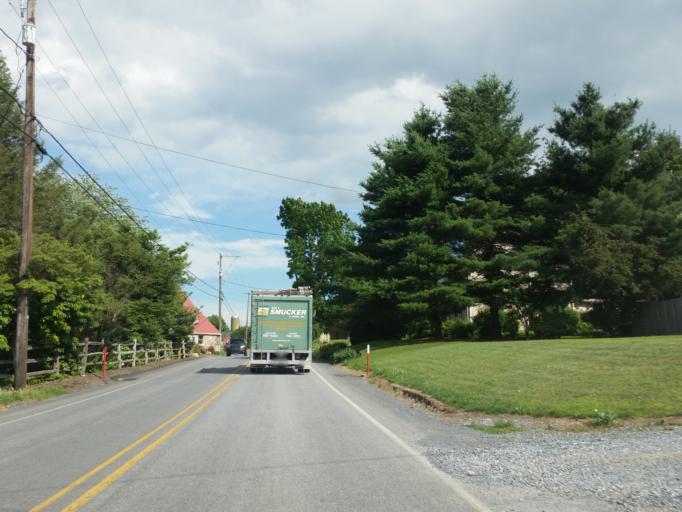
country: US
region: Pennsylvania
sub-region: Lancaster County
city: Lampeter
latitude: 40.0160
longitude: -76.2320
